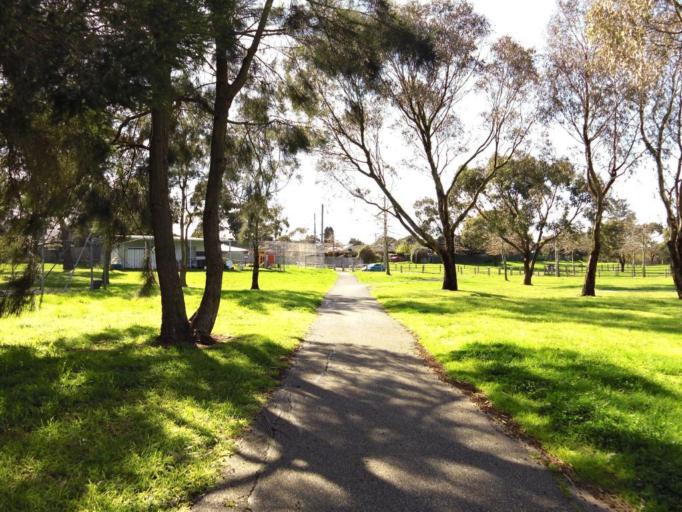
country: AU
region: Victoria
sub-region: Knox
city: Rowville
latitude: -37.9456
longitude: 145.2198
